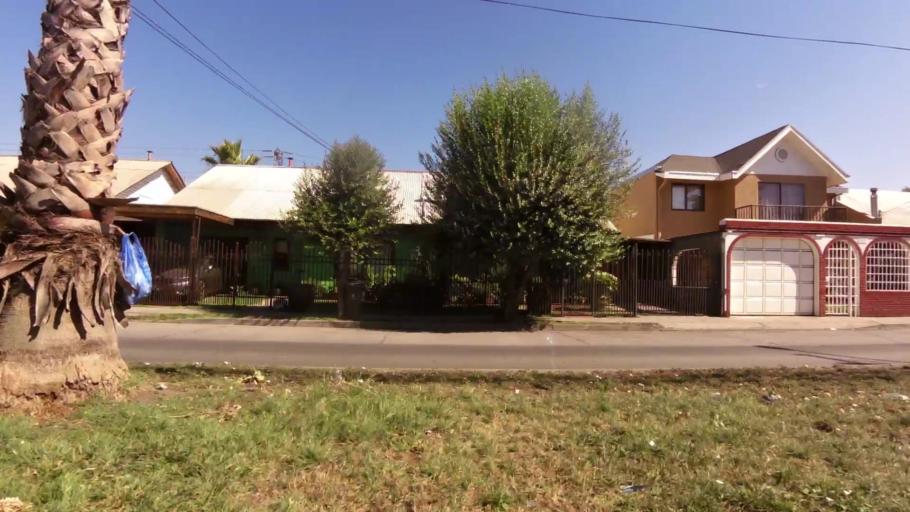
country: CL
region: Maule
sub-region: Provincia de Curico
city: Curico
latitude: -34.9739
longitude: -71.2609
